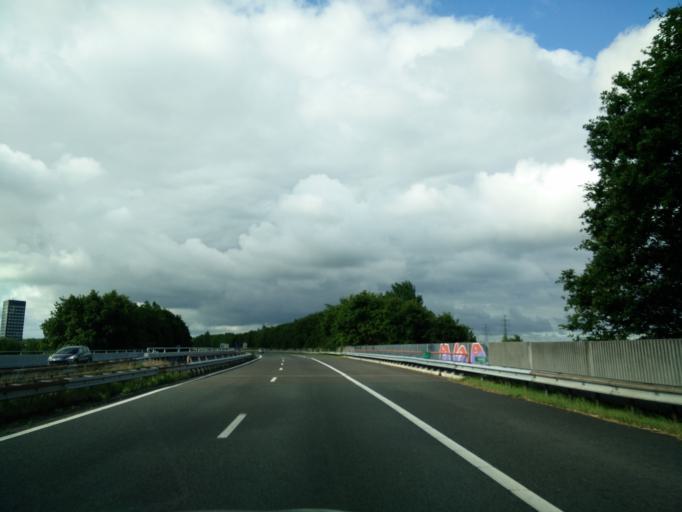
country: NL
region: Drenthe
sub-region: Gemeente Assen
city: Assen
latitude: 53.0018
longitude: 6.5270
